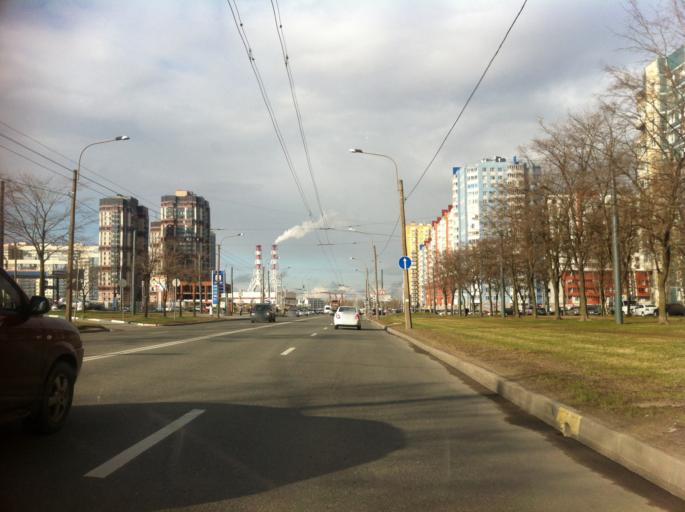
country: RU
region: St.-Petersburg
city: Uritsk
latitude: 59.8599
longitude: 30.1785
